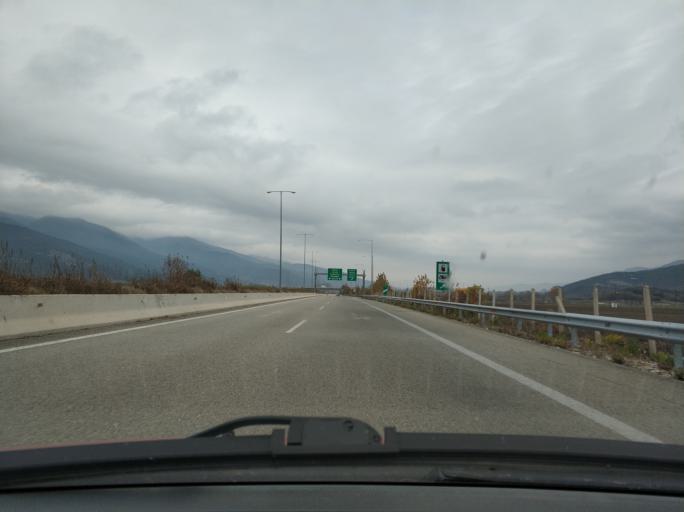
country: GR
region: East Macedonia and Thrace
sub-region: Nomos Kavalas
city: Nikisiani
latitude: 40.8362
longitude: 24.1114
